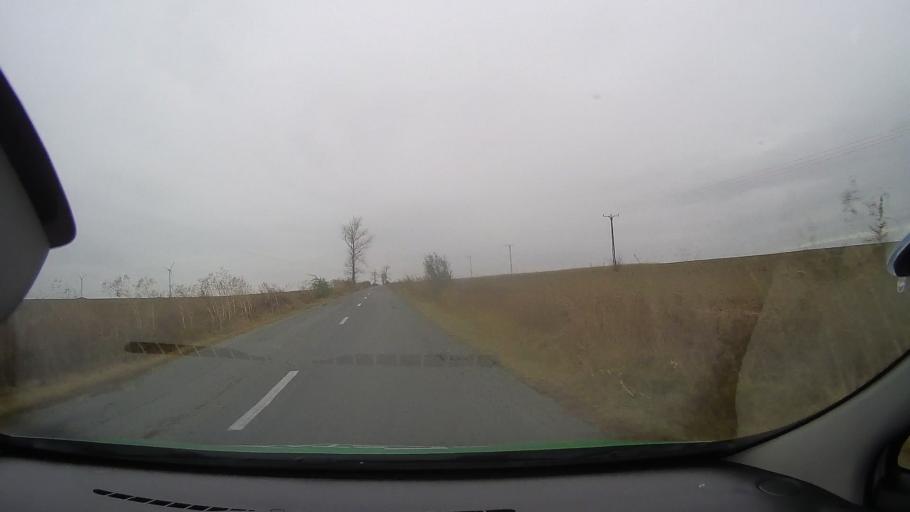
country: RO
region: Constanta
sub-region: Comuna Pantelimon
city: Pantelimon
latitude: 44.5619
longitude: 28.3210
